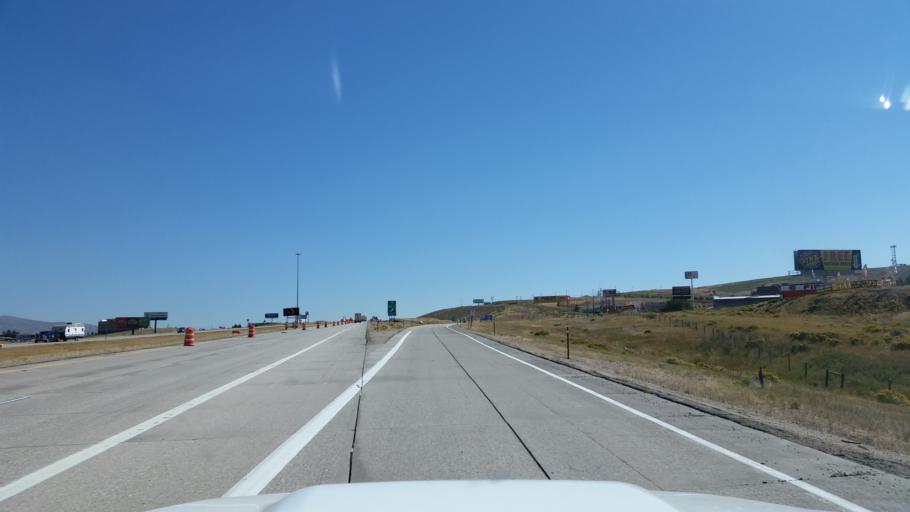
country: US
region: Wyoming
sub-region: Uinta County
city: Evanston
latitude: 41.2573
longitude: -110.9928
